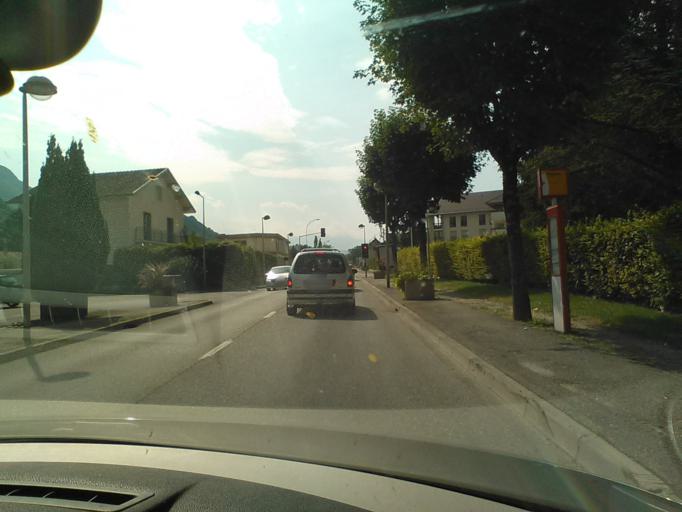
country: FR
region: Rhone-Alpes
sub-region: Departement de la Savoie
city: Challes-les-Eaux
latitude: 45.5456
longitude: 5.9868
